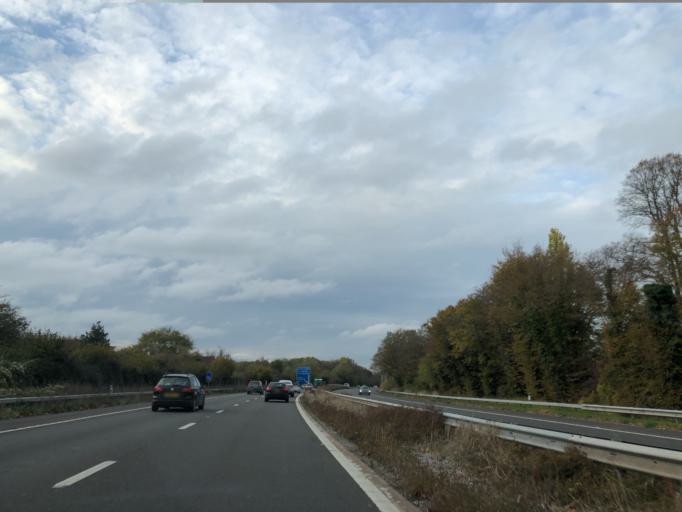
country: GB
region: England
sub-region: Royal Borough of Windsor and Maidenhead
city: White Waltham
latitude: 51.5133
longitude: -0.7586
